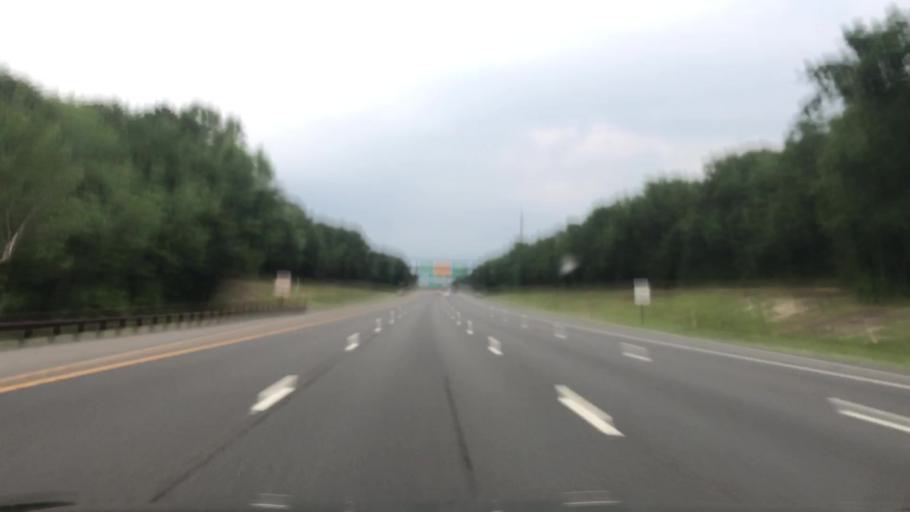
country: US
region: New Jersey
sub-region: Monmouth County
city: Shark River Hills
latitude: 40.2347
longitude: -74.0910
